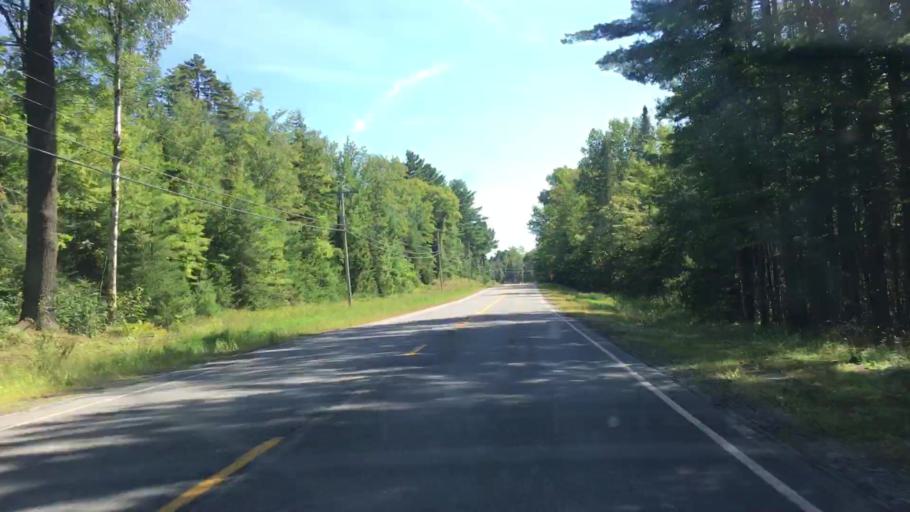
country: US
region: Maine
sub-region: Piscataquis County
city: Milo
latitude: 45.1919
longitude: -68.8988
